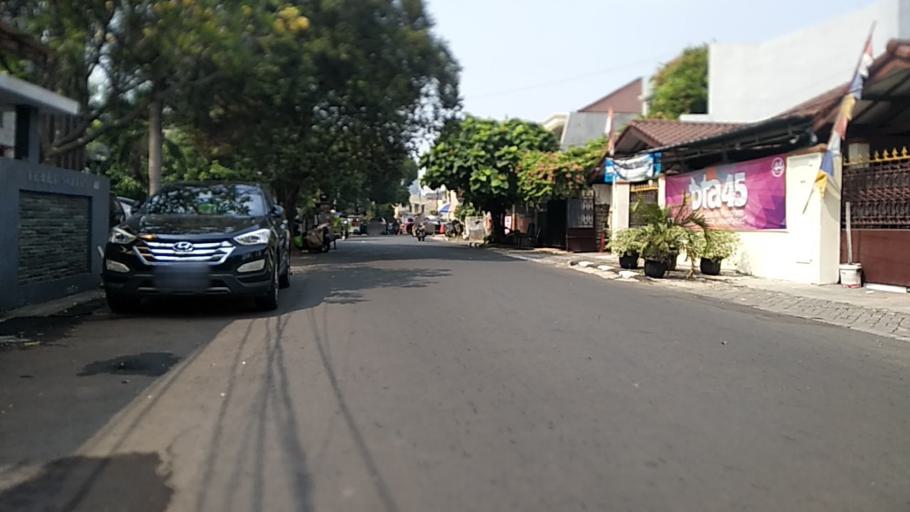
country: ID
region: Jakarta Raya
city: Jakarta
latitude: -6.2369
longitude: 106.8499
